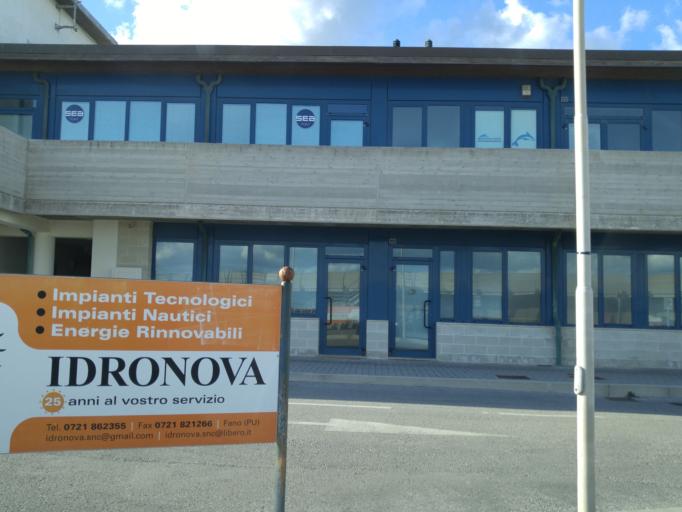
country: IT
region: The Marches
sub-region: Provincia di Pesaro e Urbino
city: Fano
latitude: 43.8526
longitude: 13.0222
